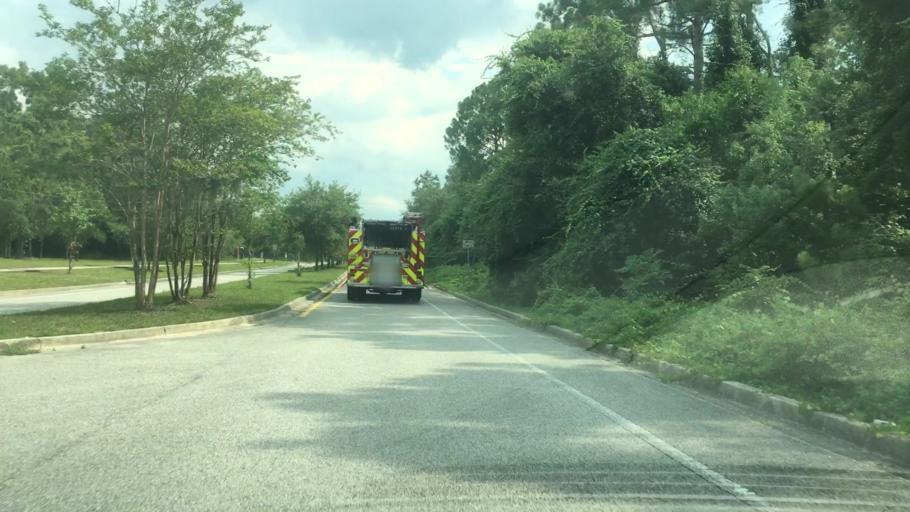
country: US
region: Florida
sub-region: Duval County
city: Neptune Beach
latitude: 30.2990
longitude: -81.5052
